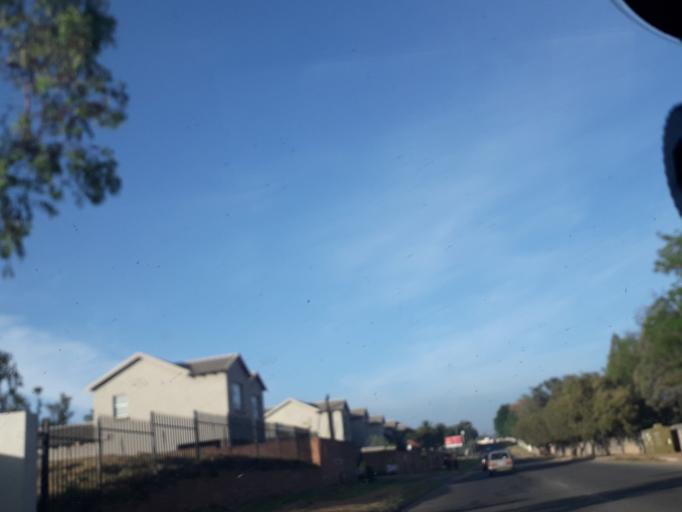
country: ZA
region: Gauteng
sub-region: City of Johannesburg Metropolitan Municipality
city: Roodepoort
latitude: -26.0892
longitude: 27.9037
